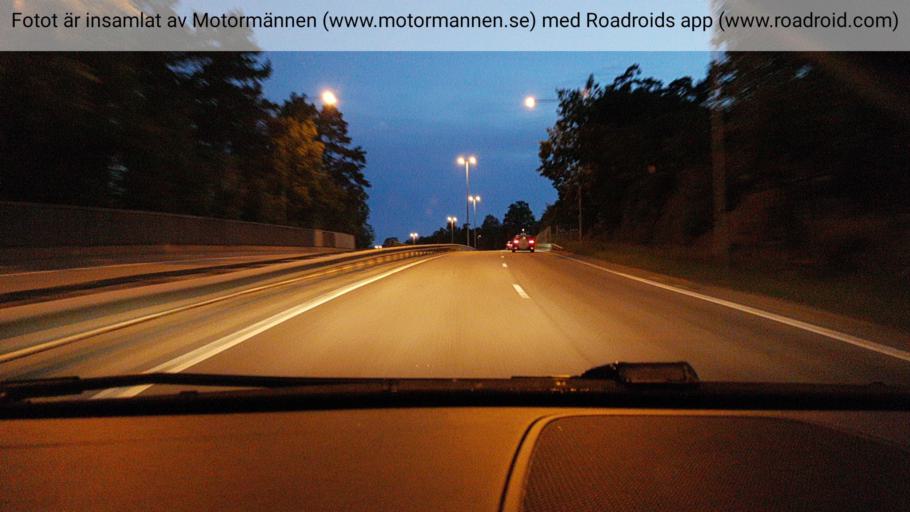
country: SE
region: Stockholm
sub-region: Huddinge Kommun
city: Huddinge
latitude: 59.2427
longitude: 17.9914
